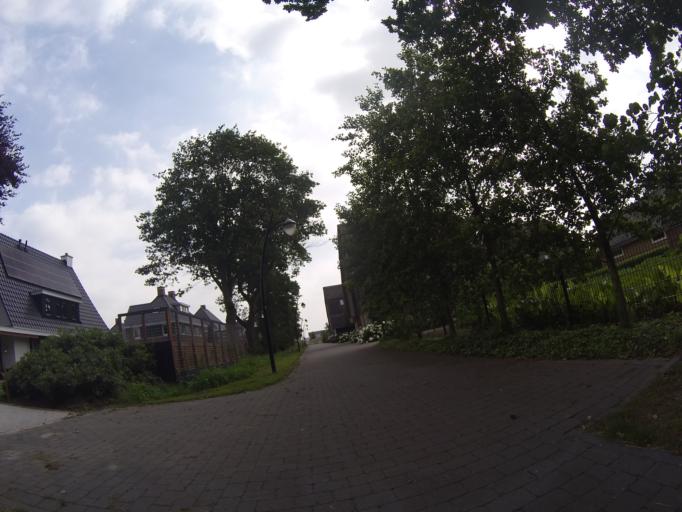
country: NL
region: Utrecht
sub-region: Gemeente Amersfoort
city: Hoogland
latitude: 52.1914
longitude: 5.4128
